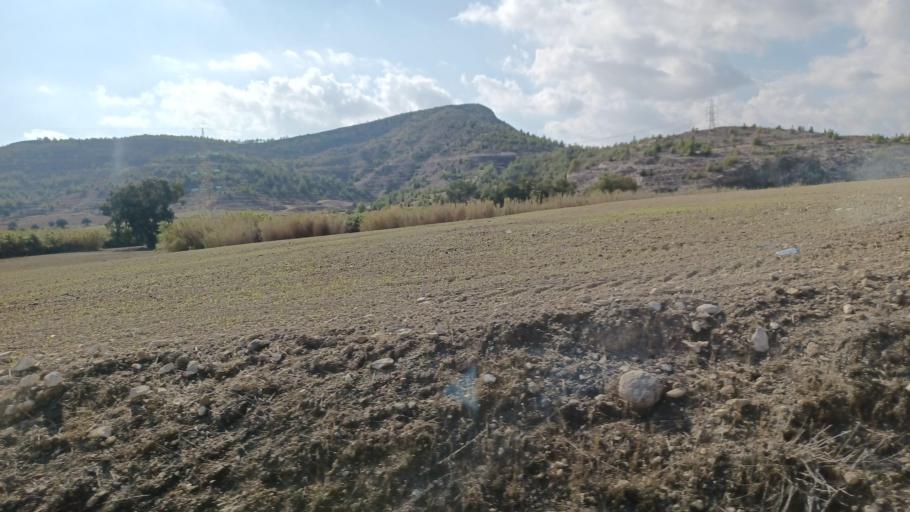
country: CY
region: Larnaka
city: Voroklini
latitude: 35.0057
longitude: 33.6491
